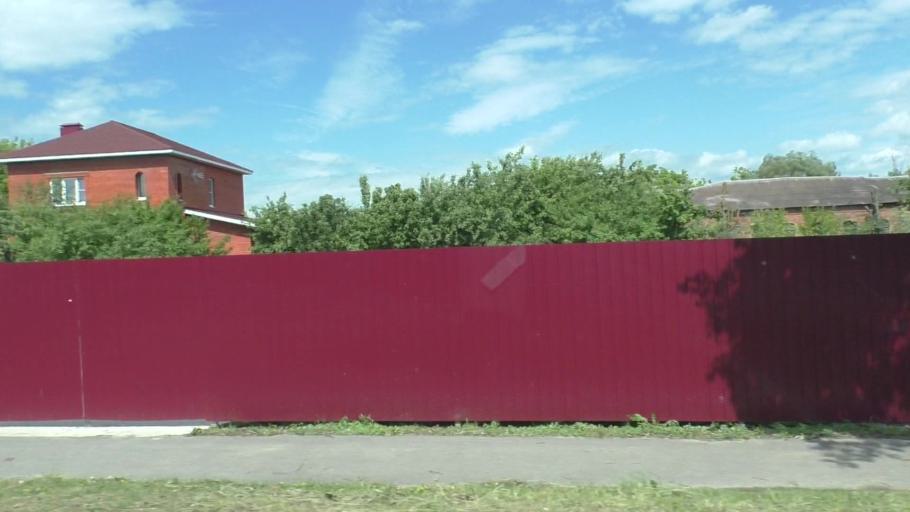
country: RU
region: Moskovskaya
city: Yegor'yevsk
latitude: 55.3862
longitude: 39.0347
